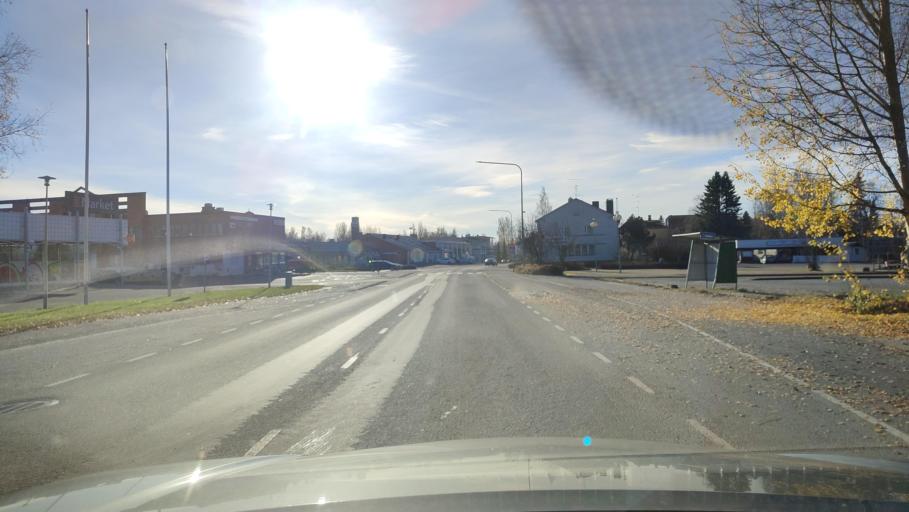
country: FI
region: Southern Ostrobothnia
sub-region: Suupohja
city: Teuva
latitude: 62.4876
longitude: 21.7466
